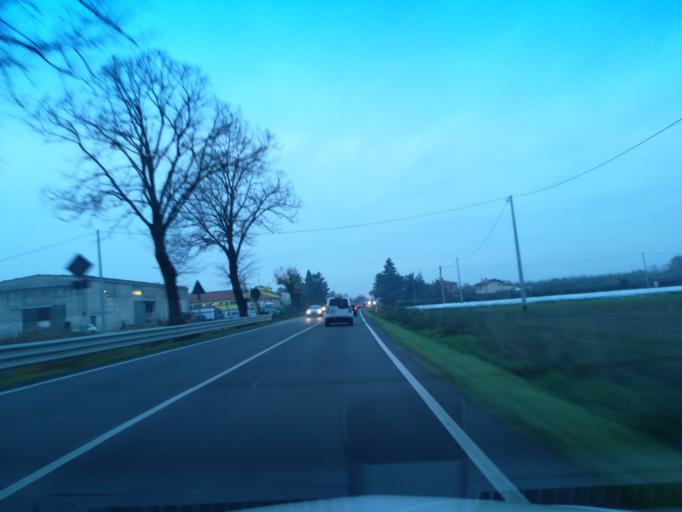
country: IT
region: Emilia-Romagna
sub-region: Provincia di Ravenna
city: Castel Bolognese
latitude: 44.3081
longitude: 11.8282
